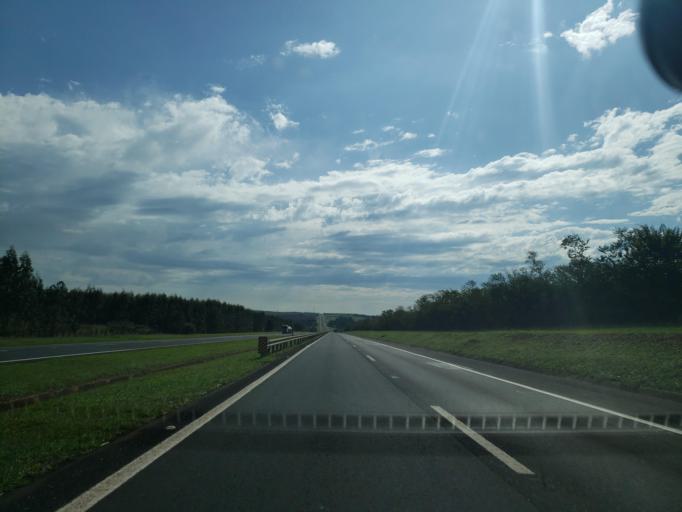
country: BR
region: Sao Paulo
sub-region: Pirajui
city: Pirajui
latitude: -21.9036
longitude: -49.5261
